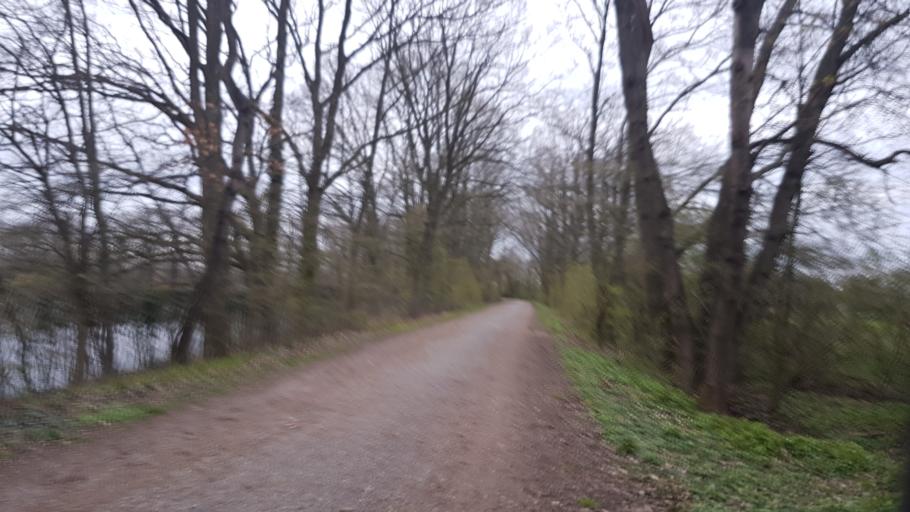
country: DE
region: Lower Saxony
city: Isernhagen Farster Bauerschaft
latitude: 52.4423
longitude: 9.8098
